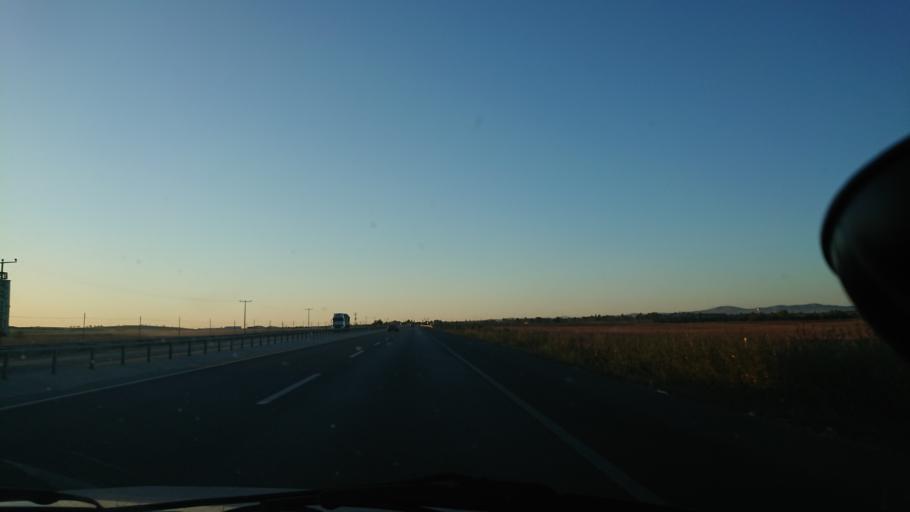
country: TR
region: Eskisehir
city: Mahmudiye
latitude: 39.5512
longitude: 30.9267
